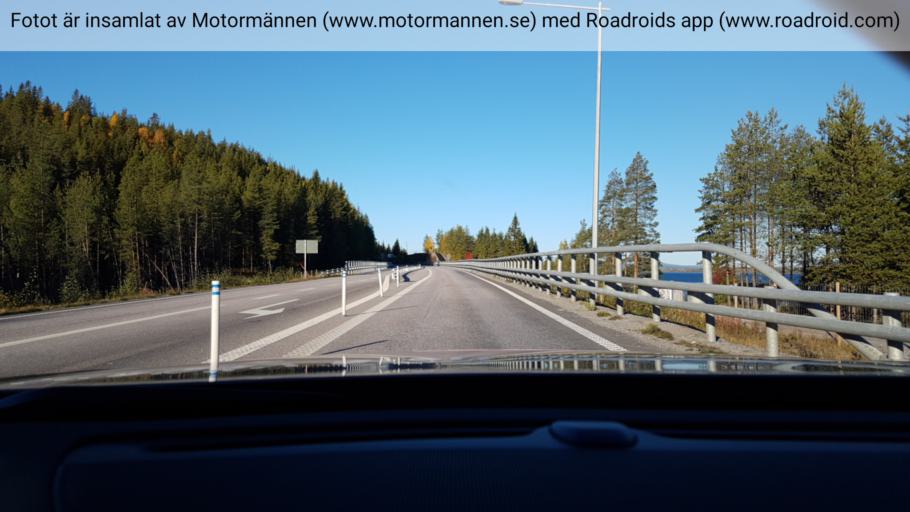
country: SE
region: Norrbotten
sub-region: Pitea Kommun
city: Bergsviken
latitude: 65.3182
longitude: 21.3731
